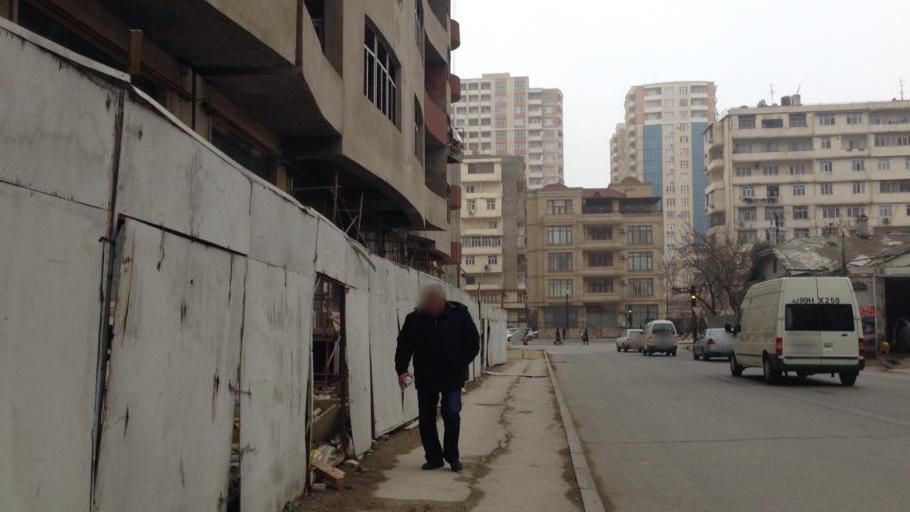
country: AZ
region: Baki
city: Baku
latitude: 40.3831
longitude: 49.8686
